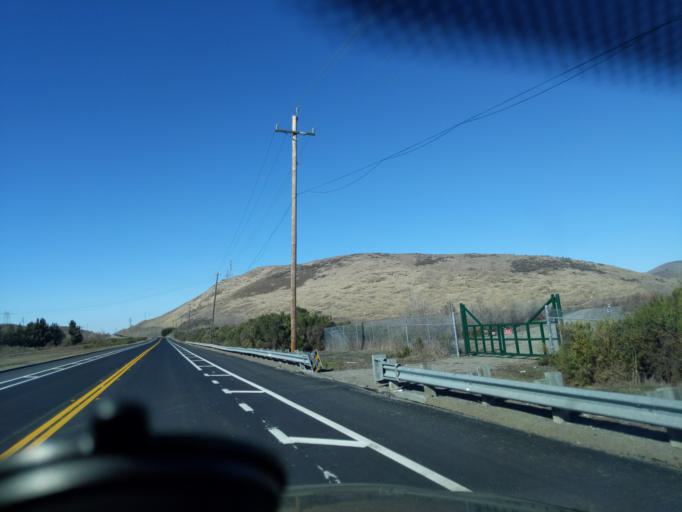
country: US
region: California
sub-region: Santa Clara County
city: Seven Trees
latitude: 37.2108
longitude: -121.7470
